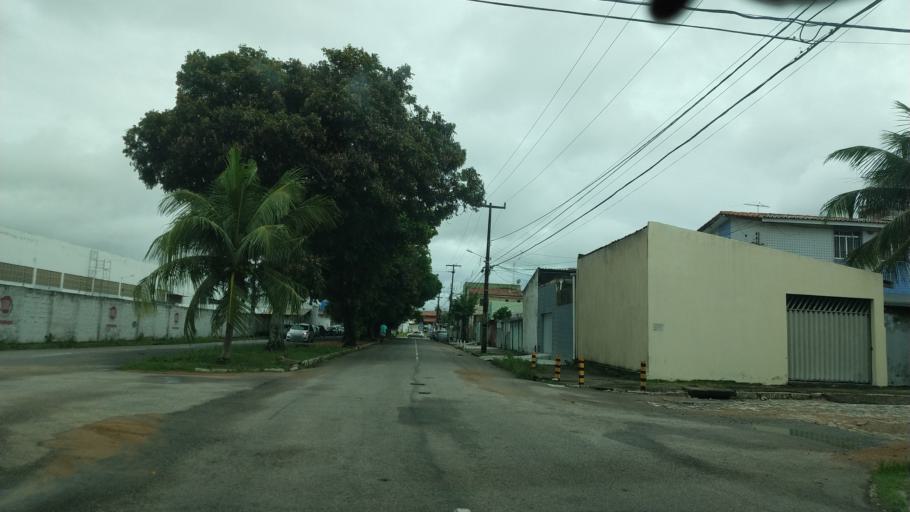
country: BR
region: Rio Grande do Norte
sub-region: Natal
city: Natal
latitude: -5.8524
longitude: -35.2012
